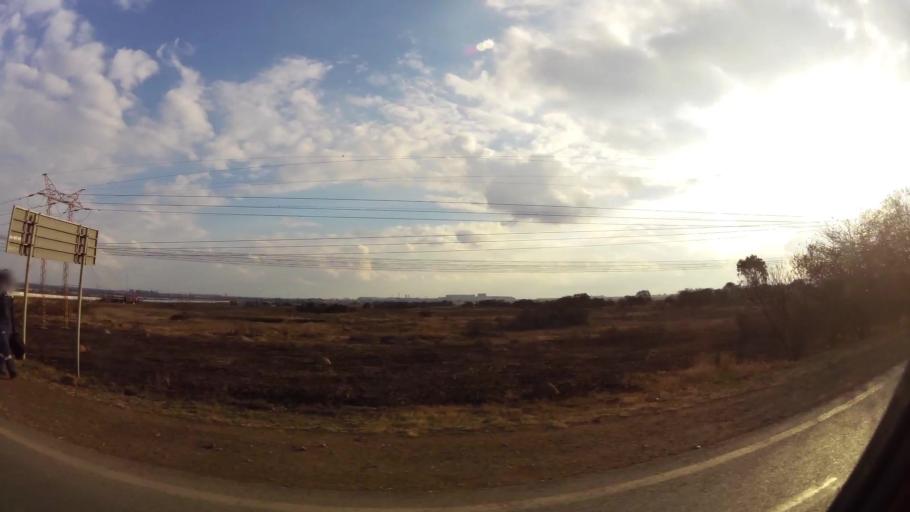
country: ZA
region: Gauteng
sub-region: Sedibeng District Municipality
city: Vereeniging
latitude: -26.6368
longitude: 27.8708
